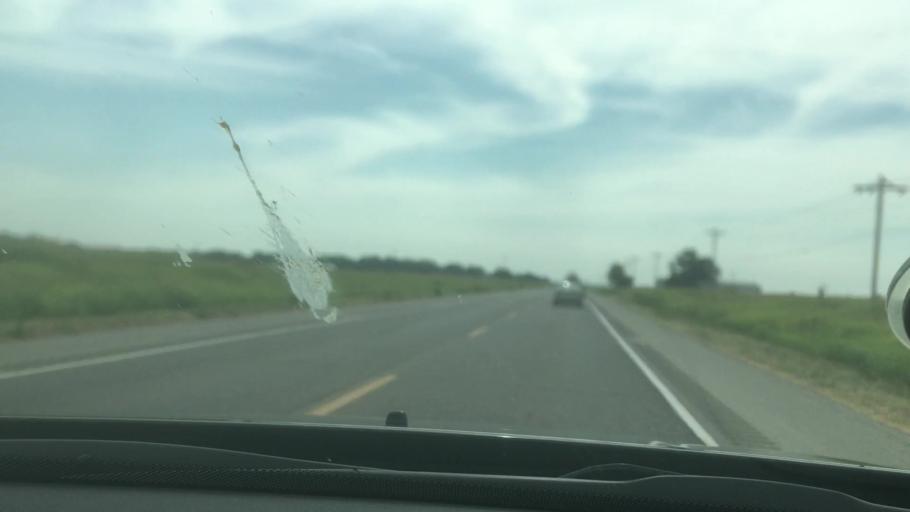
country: US
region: Oklahoma
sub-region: Garvin County
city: Lindsay
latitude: 34.8248
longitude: -97.5402
